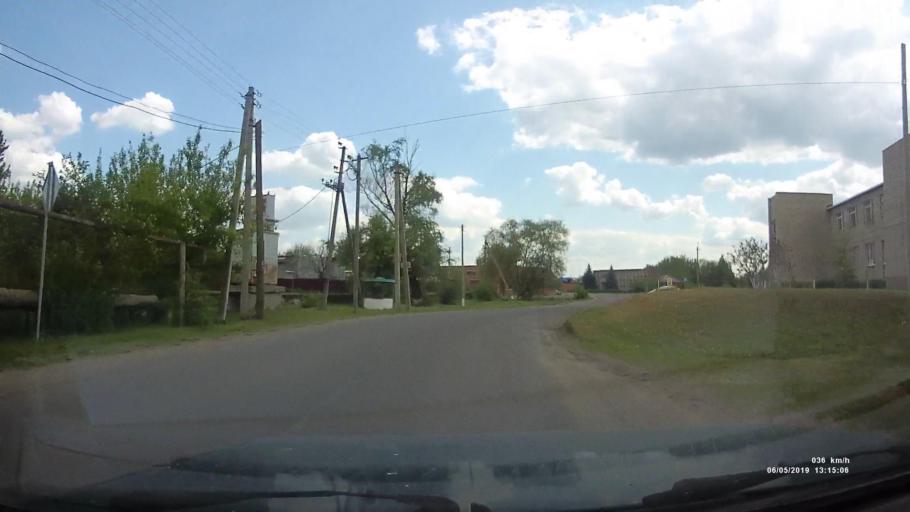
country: RU
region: Rostov
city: Ust'-Donetskiy
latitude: 47.7470
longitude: 40.9440
